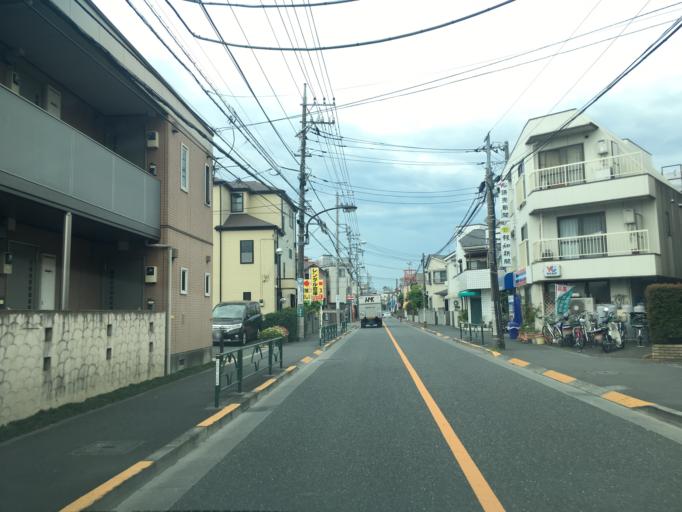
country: JP
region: Tokyo
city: Kokubunji
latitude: 35.6623
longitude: 139.4618
